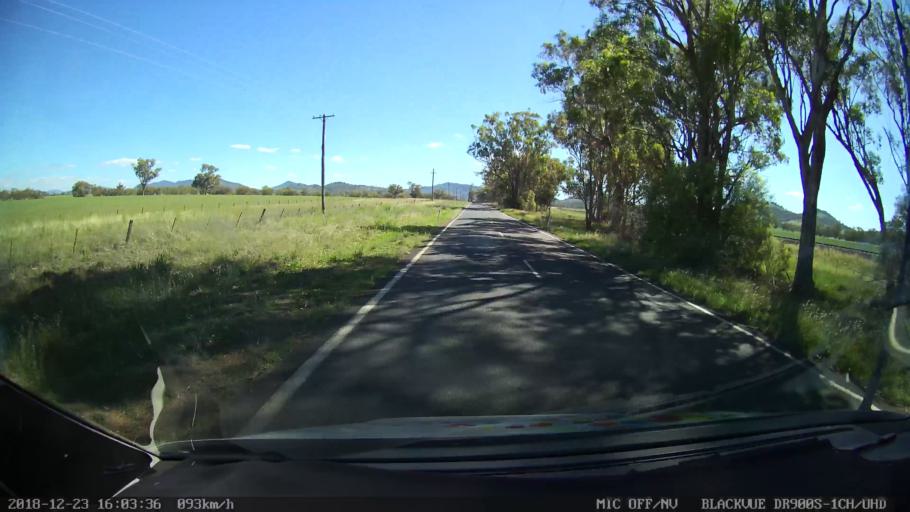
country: AU
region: New South Wales
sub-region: Tamworth Municipality
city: Phillip
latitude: -31.2453
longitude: 150.7990
